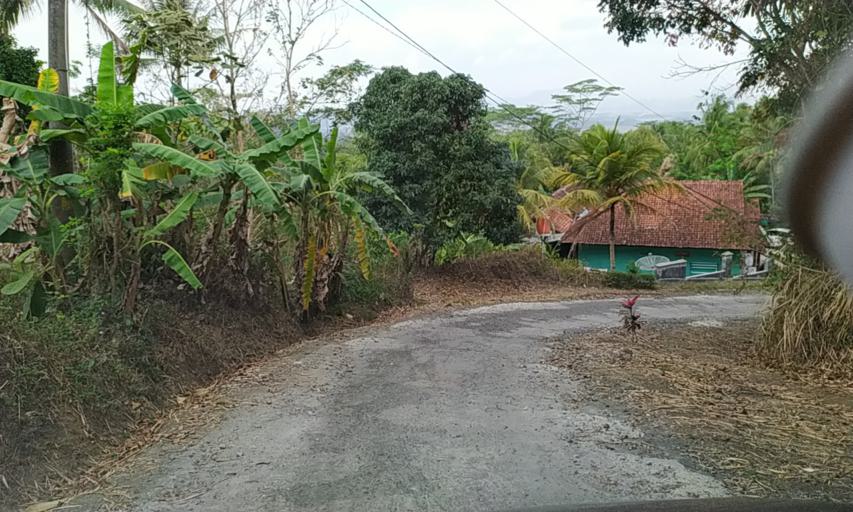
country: ID
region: Central Java
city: Batububut
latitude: -7.2897
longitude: 108.5800
